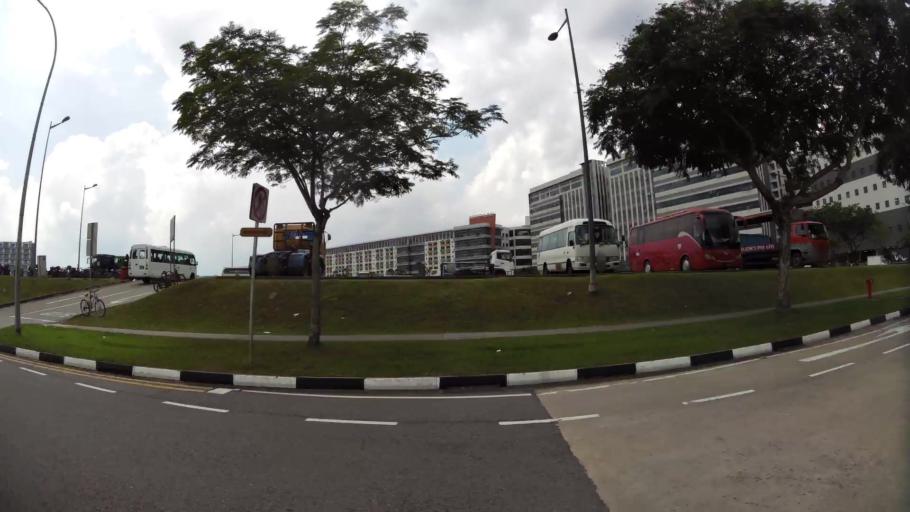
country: MY
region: Johor
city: Johor Bahru
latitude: 1.4609
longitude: 103.8157
